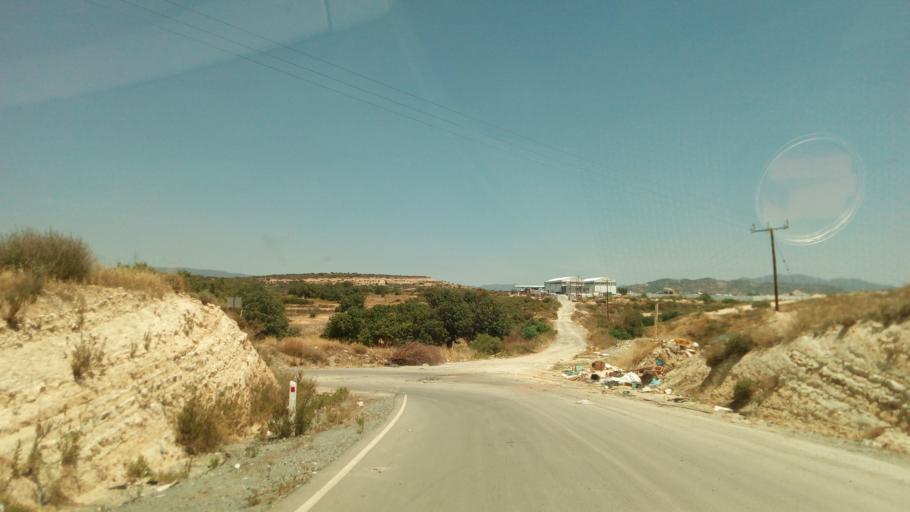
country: CY
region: Limassol
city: Ypsonas
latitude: 34.7490
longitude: 32.9472
